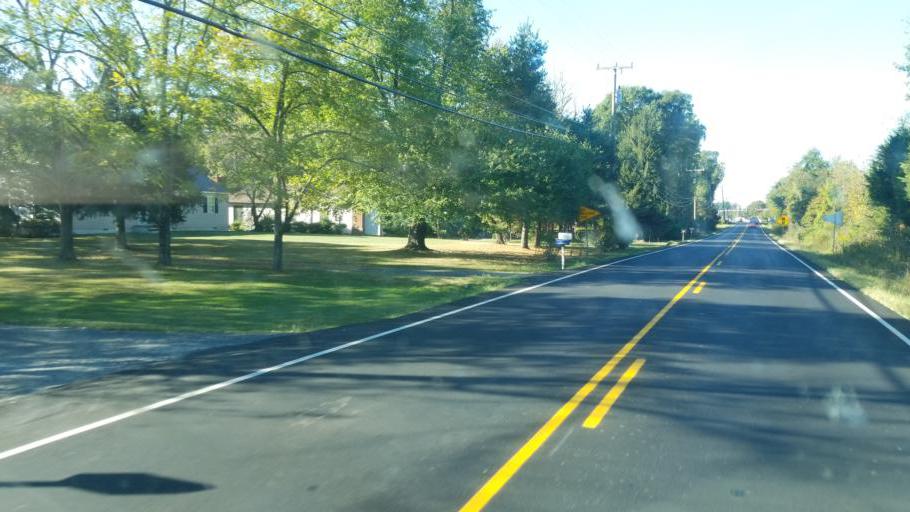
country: US
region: Virginia
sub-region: Fauquier County
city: Bealeton
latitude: 38.5649
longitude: -77.7980
